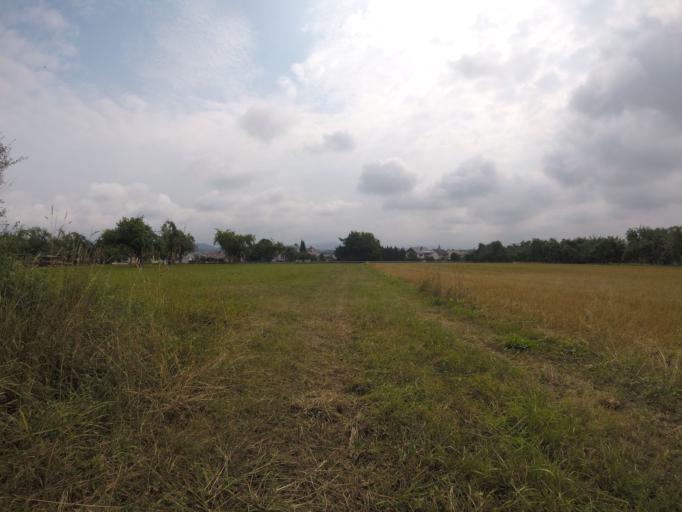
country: DE
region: Baden-Wuerttemberg
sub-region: Regierungsbezirk Stuttgart
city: Aspach
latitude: 48.9662
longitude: 9.3874
